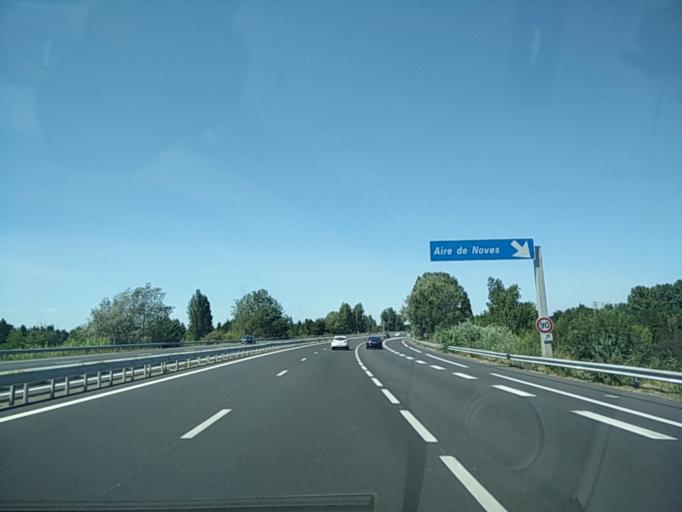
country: FR
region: Provence-Alpes-Cote d'Azur
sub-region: Departement du Vaucluse
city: Caumont-sur-Durance
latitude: 43.8783
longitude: 4.9320
